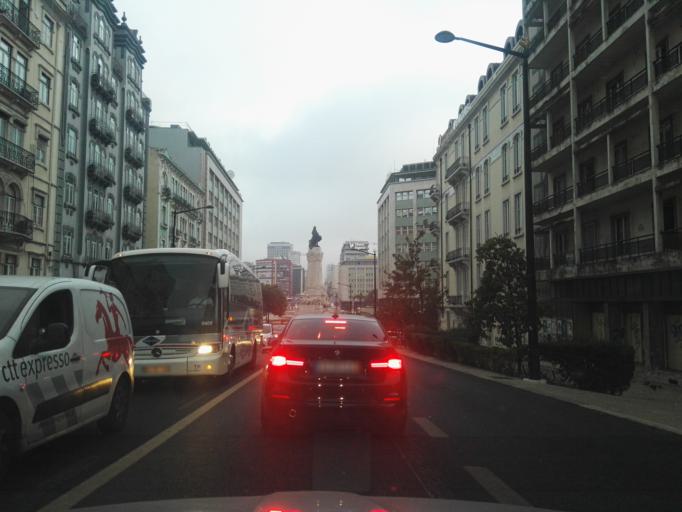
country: PT
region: Lisbon
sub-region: Lisbon
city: Lisbon
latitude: 38.7235
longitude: -9.1511
